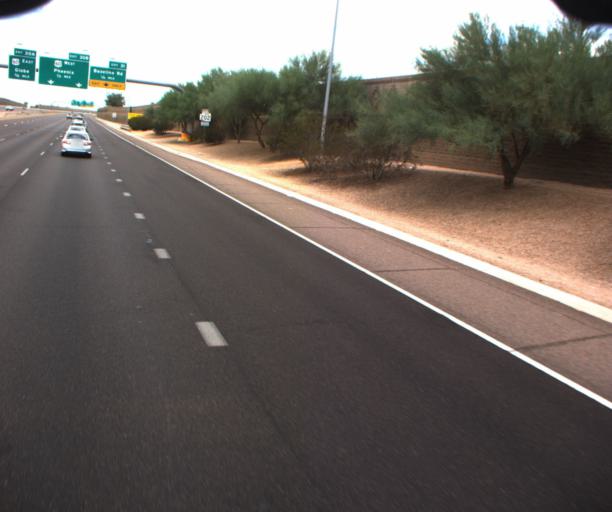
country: US
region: Arizona
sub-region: Pinal County
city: Apache Junction
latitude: 33.3702
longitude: -111.6453
